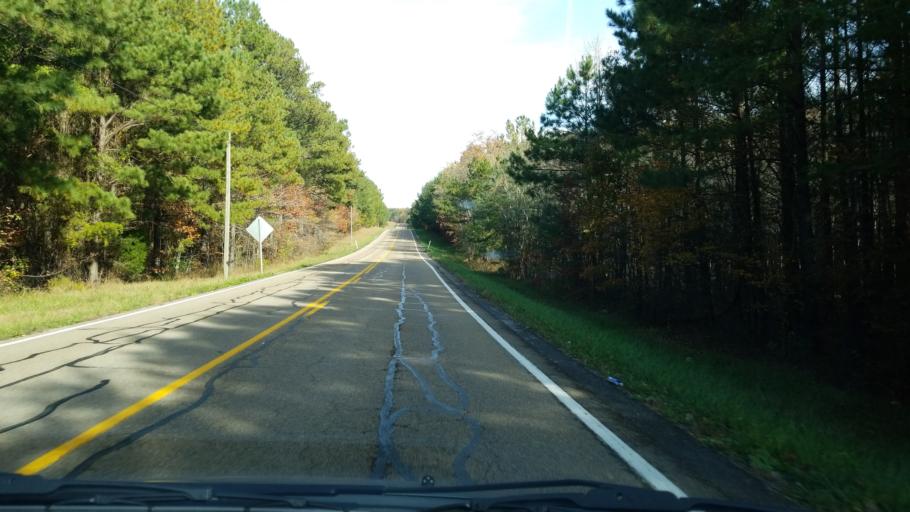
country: US
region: Tennessee
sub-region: Sequatchie County
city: Dunlap
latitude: 35.4580
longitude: -85.4943
